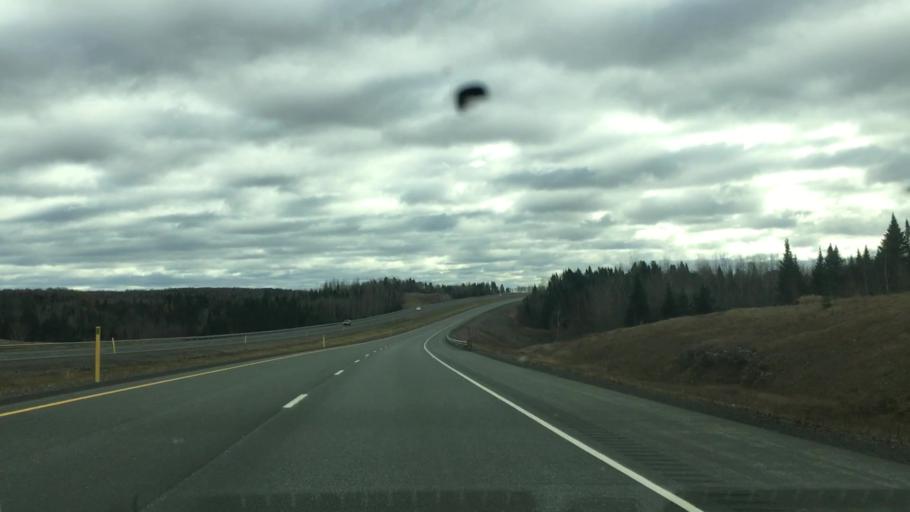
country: CA
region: New Brunswick
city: Florenceville-Bristol
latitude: 46.5420
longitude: -67.7153
